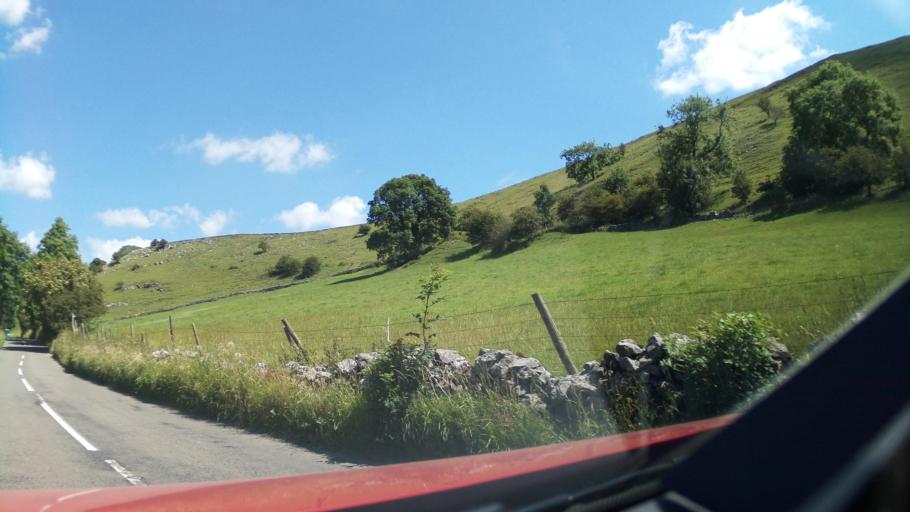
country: GB
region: England
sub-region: Derbyshire
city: Buxton
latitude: 53.1979
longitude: -1.8752
